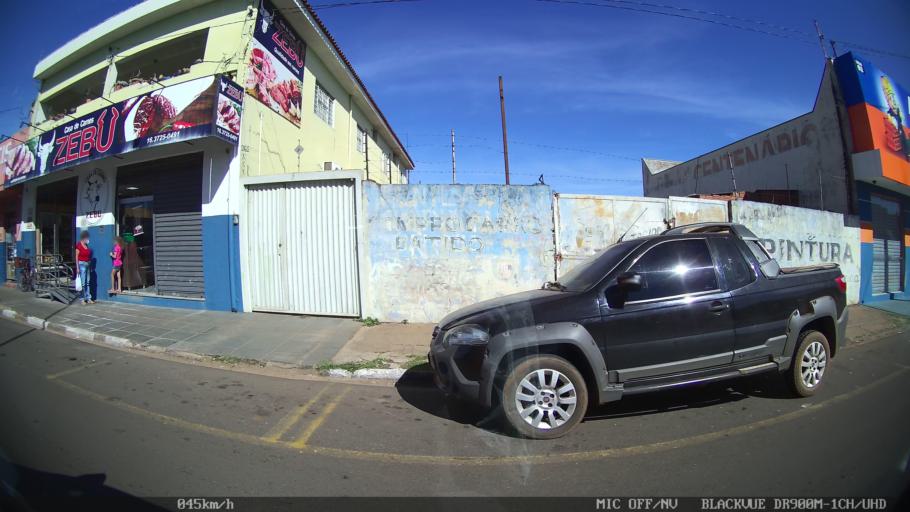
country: BR
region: Sao Paulo
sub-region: Franca
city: Franca
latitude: -20.5341
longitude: -47.3655
